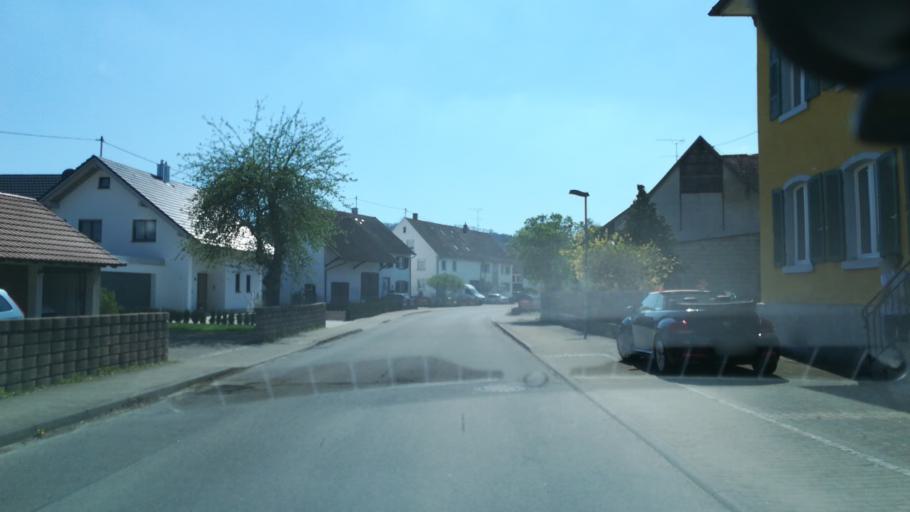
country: DE
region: Baden-Wuerttemberg
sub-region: Freiburg Region
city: Muhlhausen-Ehingen
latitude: 47.8238
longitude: 8.8010
